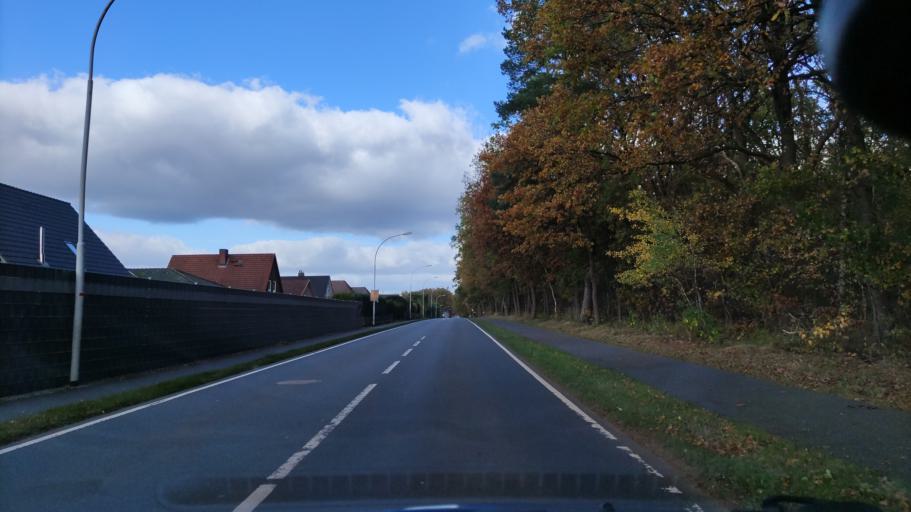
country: DE
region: Lower Saxony
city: Munster
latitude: 53.0044
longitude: 10.0885
